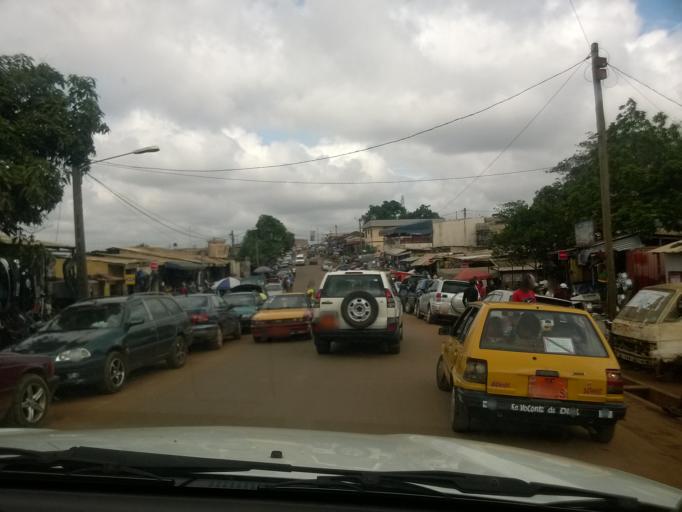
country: CM
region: Centre
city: Yaounde
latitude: 3.8652
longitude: 11.5307
